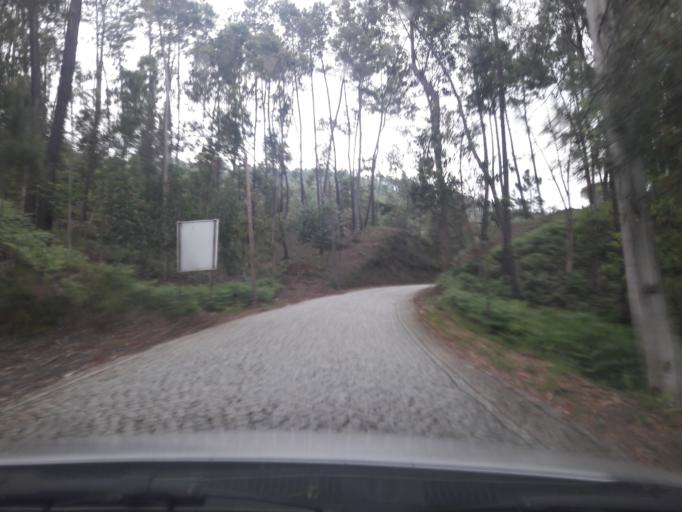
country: PT
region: Porto
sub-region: Amarante
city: Teloes
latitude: 41.3402
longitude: -8.0698
